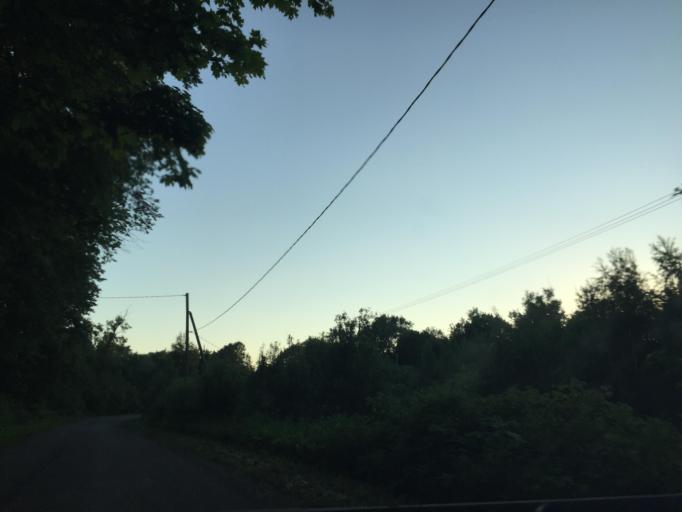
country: LV
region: Rezekne
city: Rezekne
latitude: 56.3794
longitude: 27.4214
